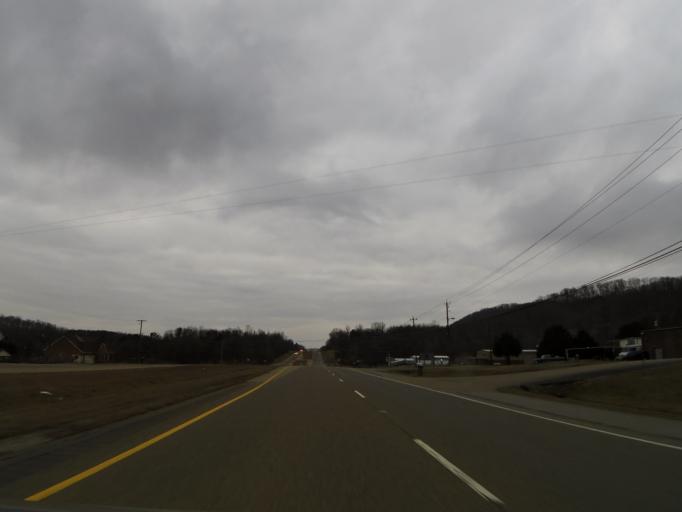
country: US
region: Tennessee
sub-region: Knox County
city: Mascot
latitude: 36.1059
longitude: -83.7408
